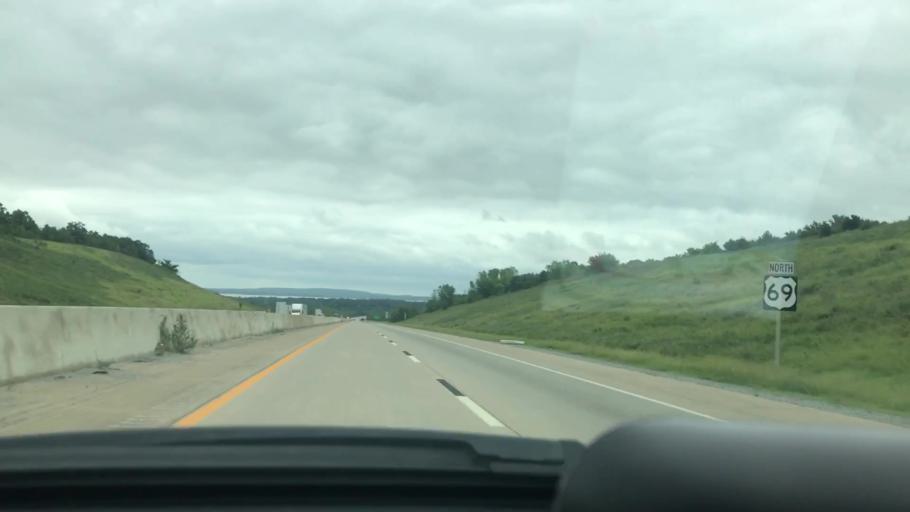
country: US
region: Oklahoma
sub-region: McIntosh County
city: Eufaula
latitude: 35.1777
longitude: -95.6457
